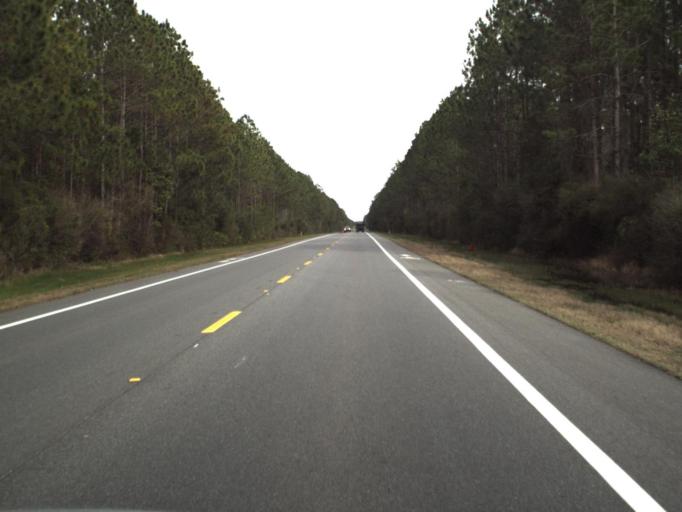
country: US
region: Florida
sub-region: Bay County
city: Callaway
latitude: 30.1527
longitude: -85.5165
